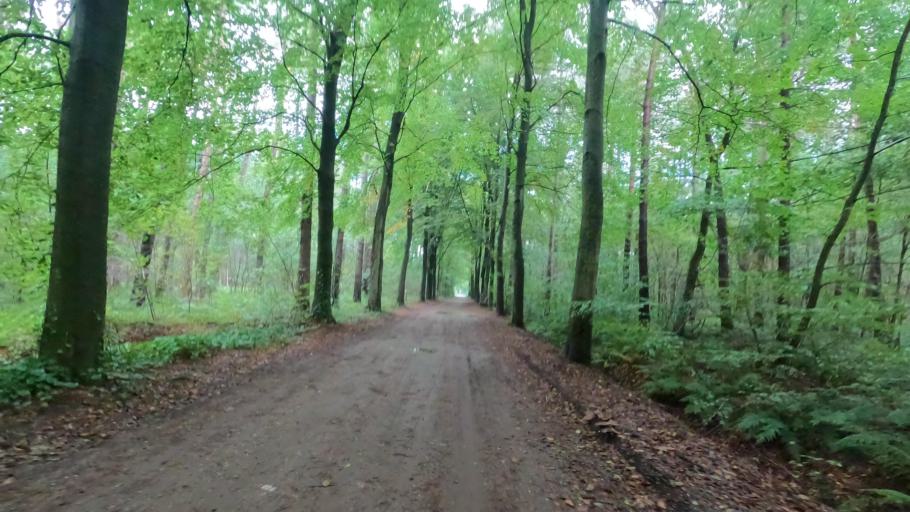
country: BE
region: Flanders
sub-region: Provincie Antwerpen
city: Schilde
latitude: 51.2340
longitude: 4.6003
